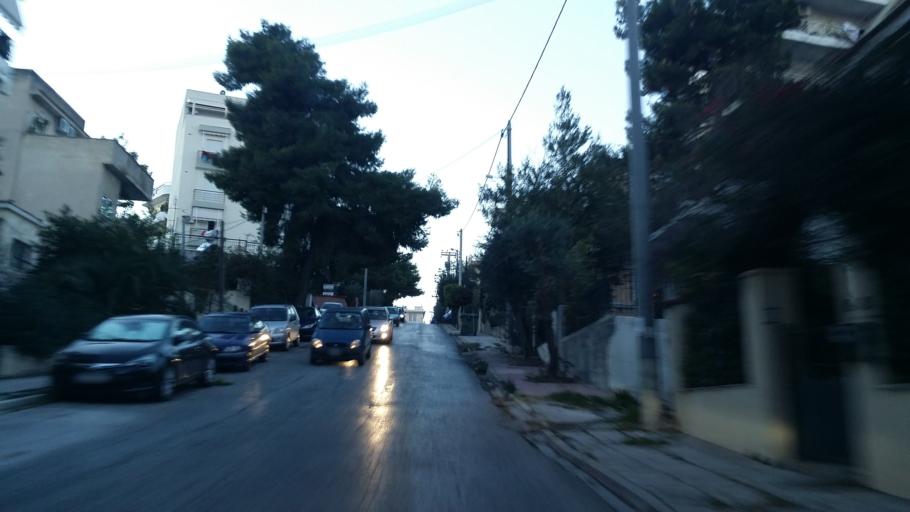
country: GR
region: Attica
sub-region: Nomarchia Athinas
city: Irakleio
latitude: 38.0541
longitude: 23.7631
